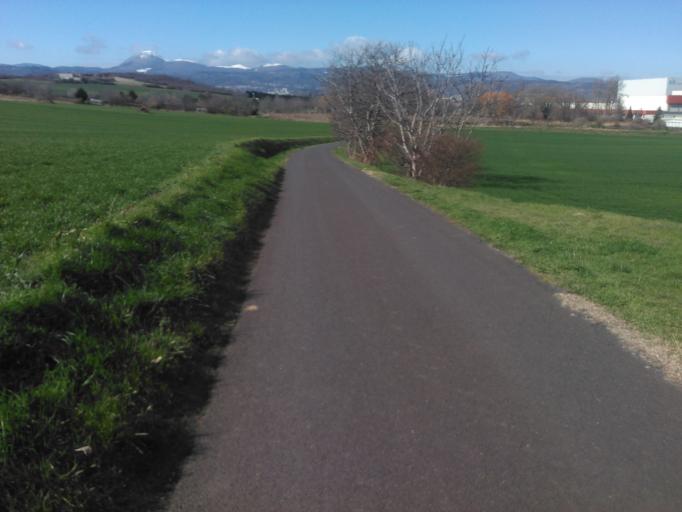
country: FR
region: Auvergne
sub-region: Departement du Puy-de-Dome
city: Aulnat
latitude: 45.7757
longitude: 3.1686
